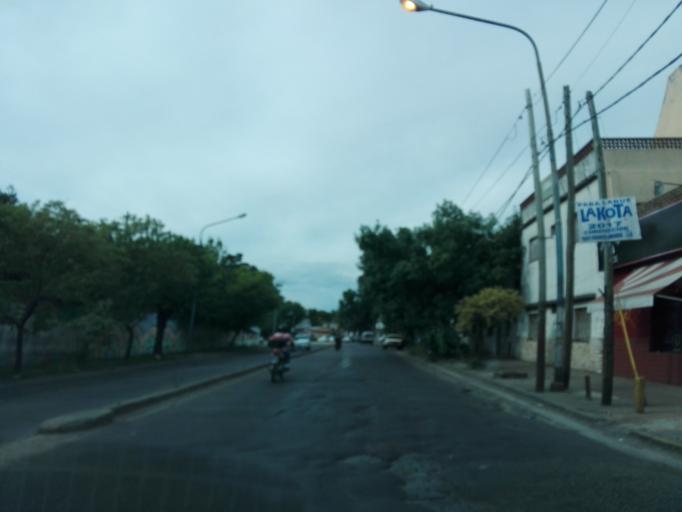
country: AR
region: Buenos Aires
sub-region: Partido de Lanus
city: Lanus
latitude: -34.7268
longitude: -58.3900
